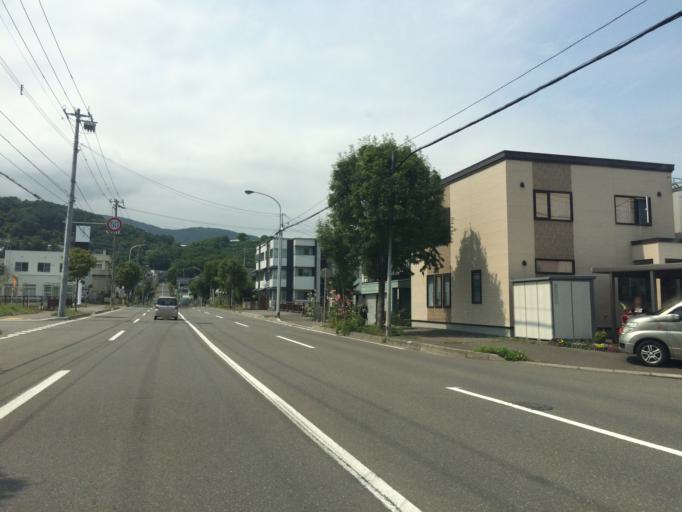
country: JP
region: Hokkaido
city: Sapporo
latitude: 43.0735
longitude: 141.2670
